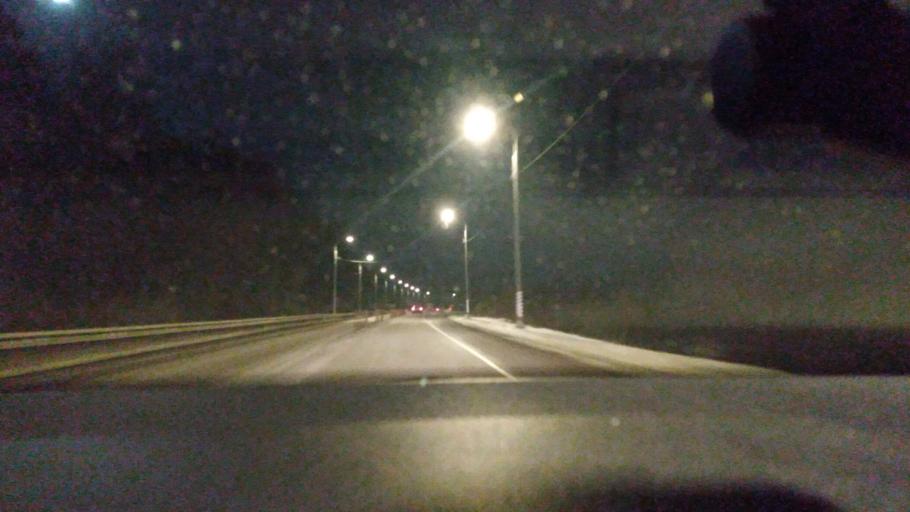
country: RU
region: Moskovskaya
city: Yegor'yevsk
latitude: 55.4493
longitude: 39.0070
